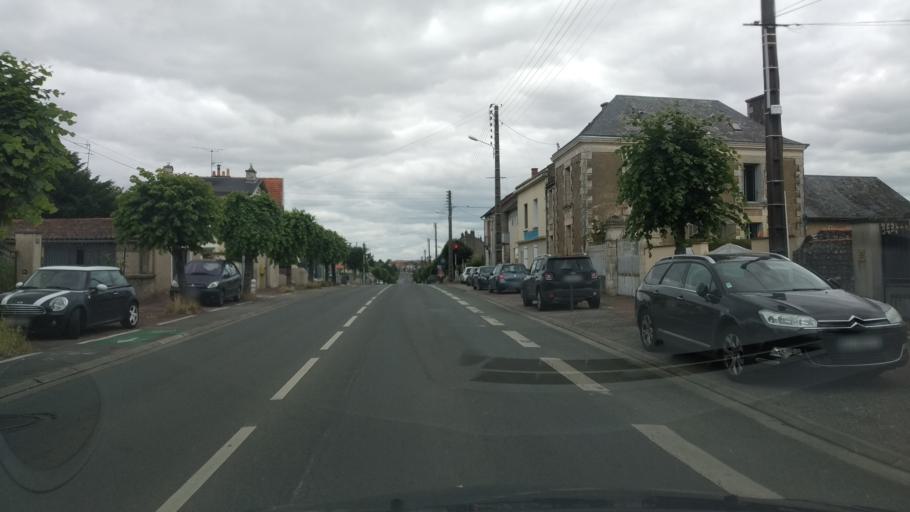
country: FR
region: Poitou-Charentes
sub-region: Departement de la Vienne
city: Poitiers
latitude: 46.5919
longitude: 0.3289
